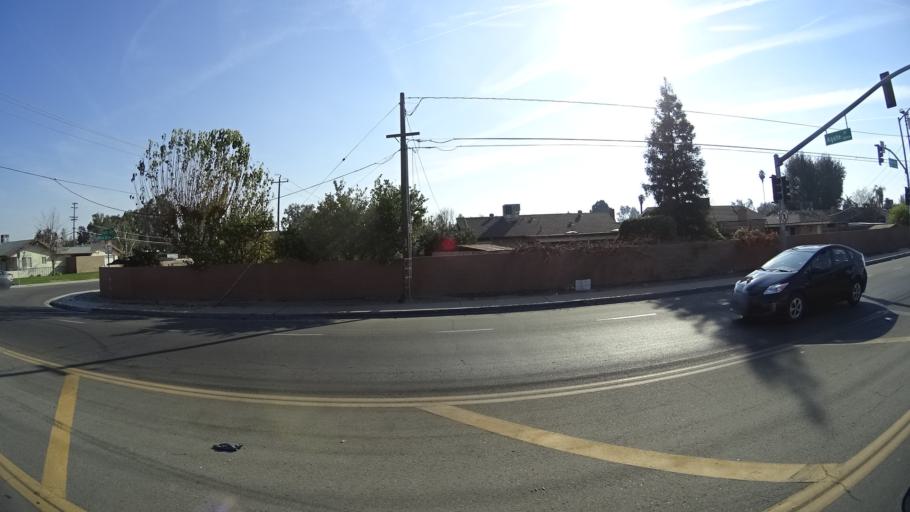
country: US
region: California
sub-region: Kern County
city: Bakersfield
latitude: 35.3250
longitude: -119.0348
